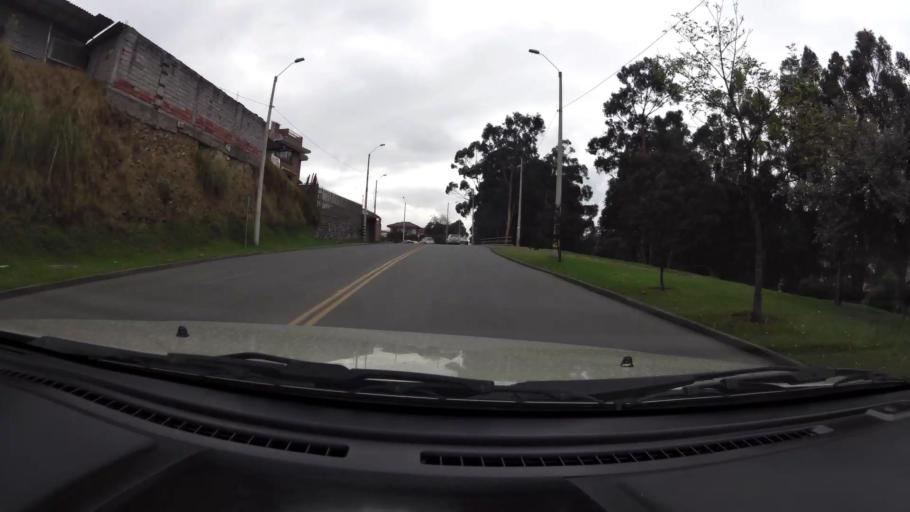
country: EC
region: Azuay
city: Cuenca
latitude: -2.9089
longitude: -79.0179
